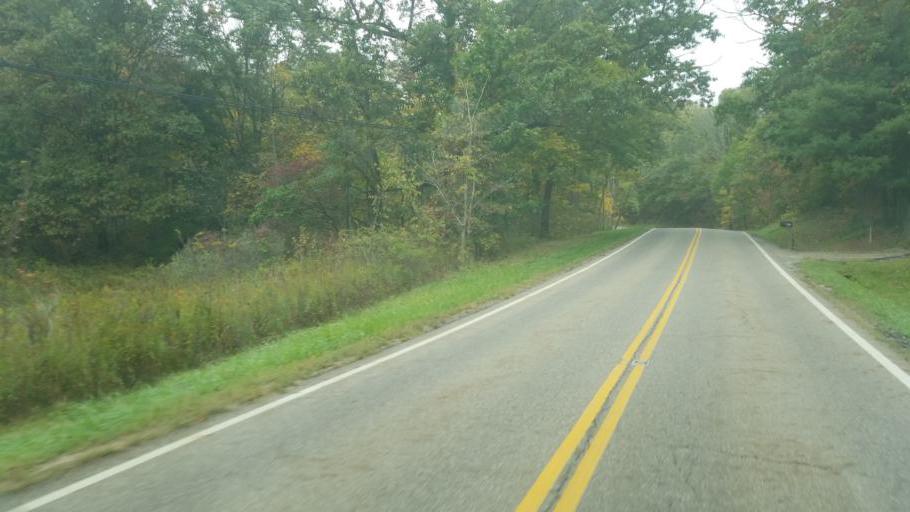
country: US
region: Ohio
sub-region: Carroll County
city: Lake Mohawk
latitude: 40.5938
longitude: -81.2634
